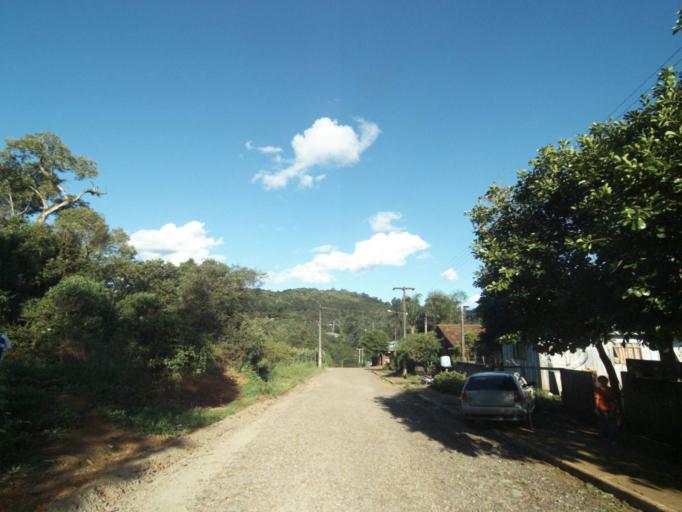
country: BR
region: Parana
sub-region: Uniao Da Vitoria
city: Uniao da Vitoria
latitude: -26.1593
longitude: -51.5343
